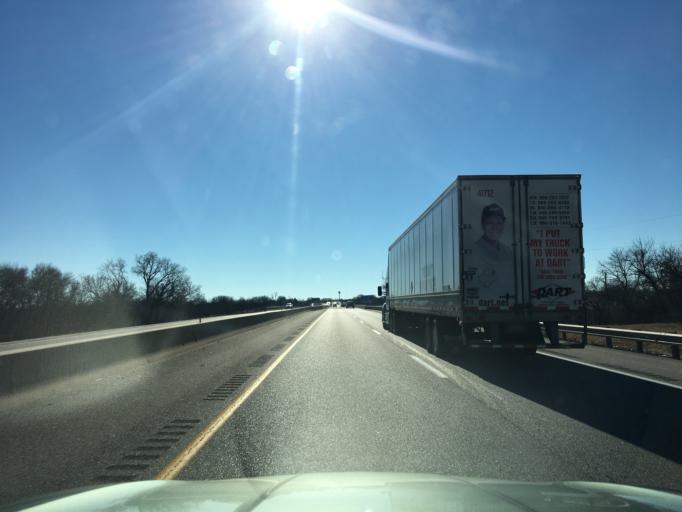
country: US
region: Kansas
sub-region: Sumner County
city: Belle Plaine
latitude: 37.3844
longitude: -97.3246
